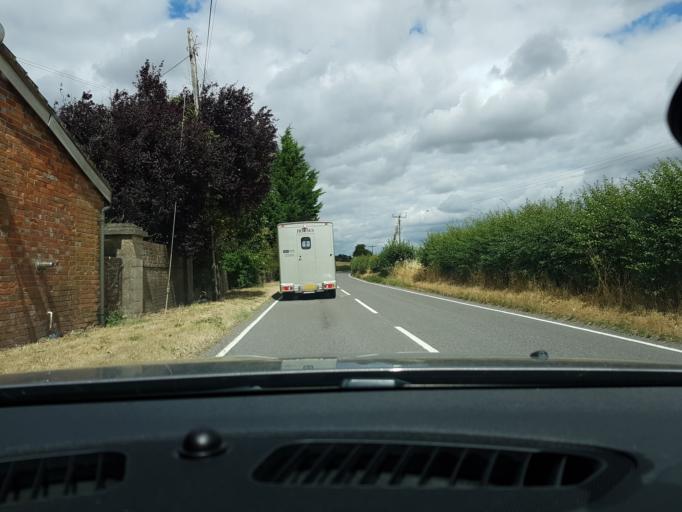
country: GB
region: England
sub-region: West Berkshire
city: Welford
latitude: 51.4869
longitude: -1.4369
